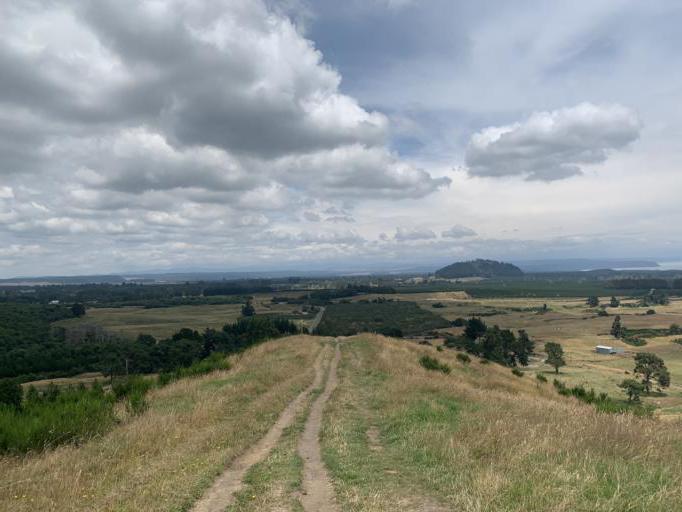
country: NZ
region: Waikato
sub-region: Taupo District
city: Taupo
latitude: -38.7008
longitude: 176.1423
